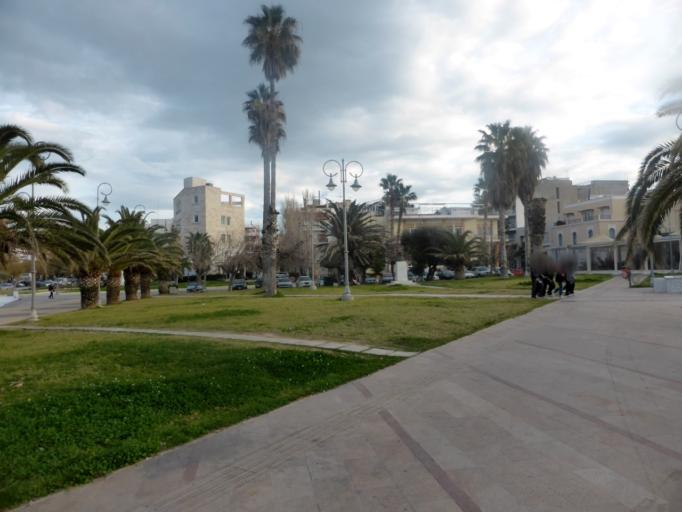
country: GR
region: Peloponnese
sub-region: Nomos Korinthias
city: Korinthos
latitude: 37.9407
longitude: 22.9348
